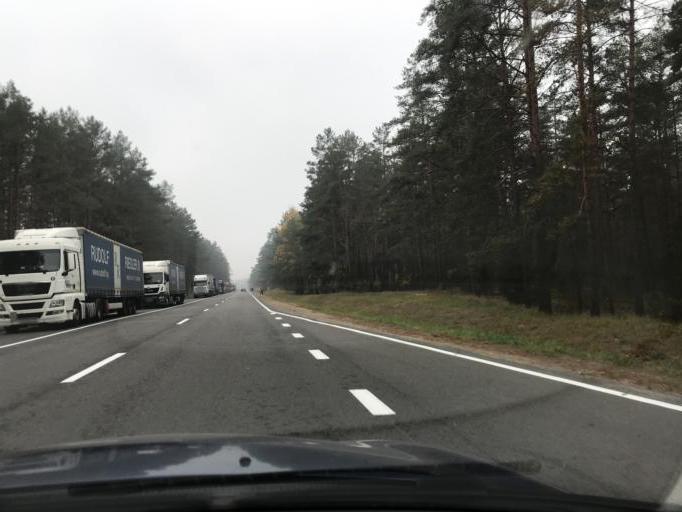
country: LT
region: Alytaus apskritis
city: Druskininkai
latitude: 53.9278
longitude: 23.9357
